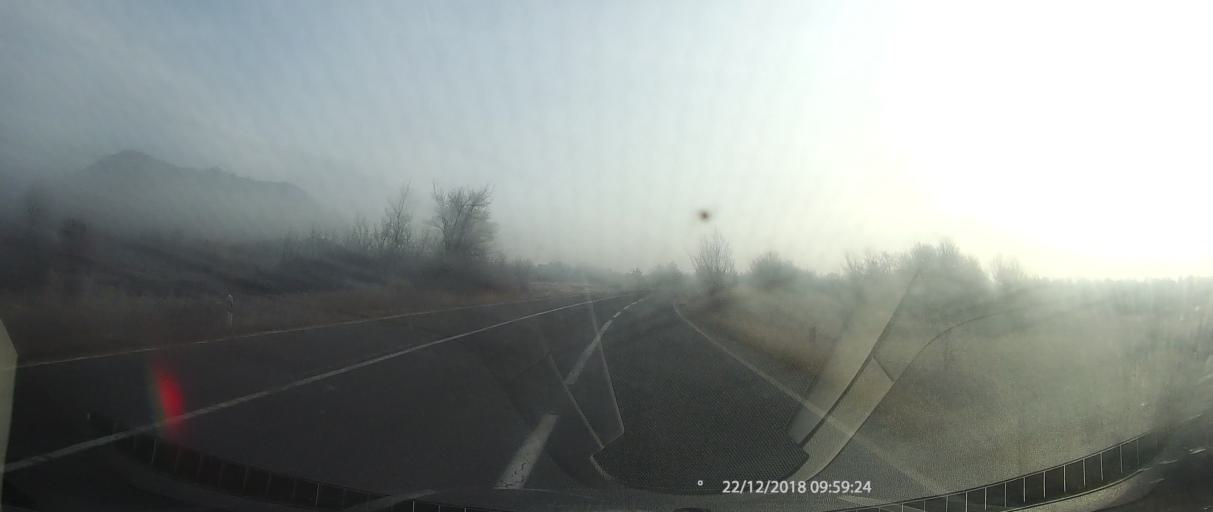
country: MK
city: Klechovce
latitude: 42.1514
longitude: 21.9583
